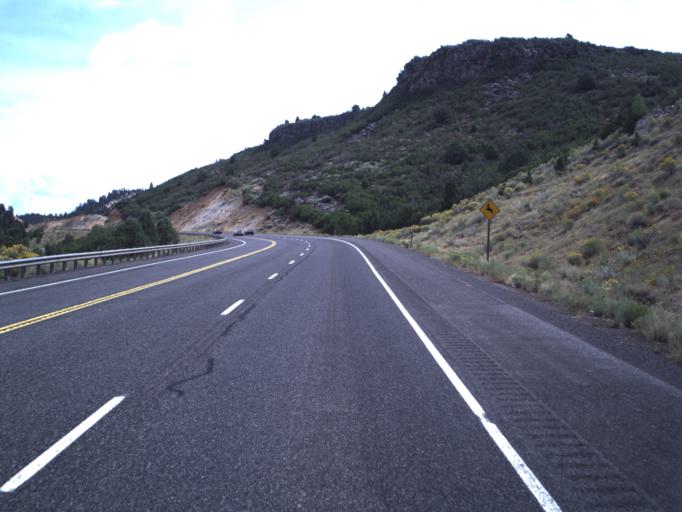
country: US
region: Utah
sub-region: Kane County
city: Kanab
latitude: 37.3850
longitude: -112.5723
